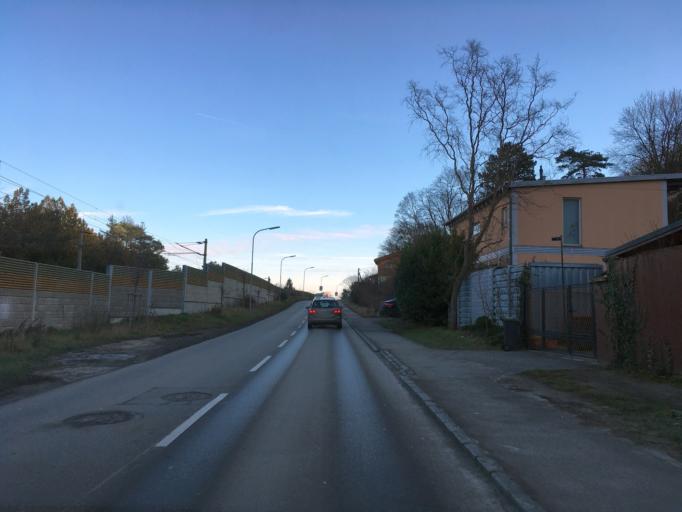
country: AT
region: Lower Austria
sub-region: Politischer Bezirk Korneuburg
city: Spillern
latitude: 48.3483
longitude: 16.2815
